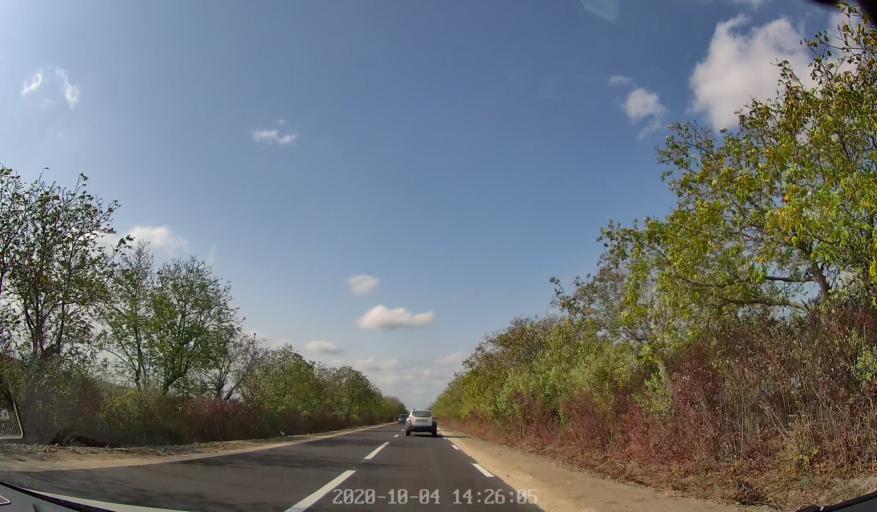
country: MD
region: Rezina
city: Saharna
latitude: 47.6244
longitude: 28.8898
